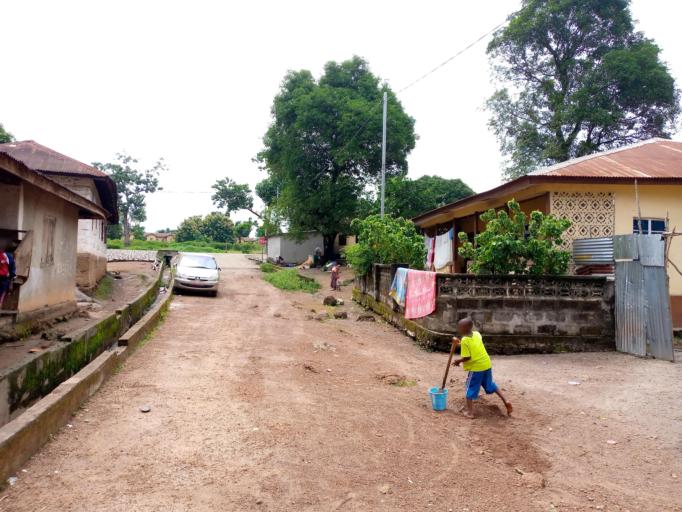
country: SL
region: Northern Province
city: Magburaka
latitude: 8.7182
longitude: -11.9388
